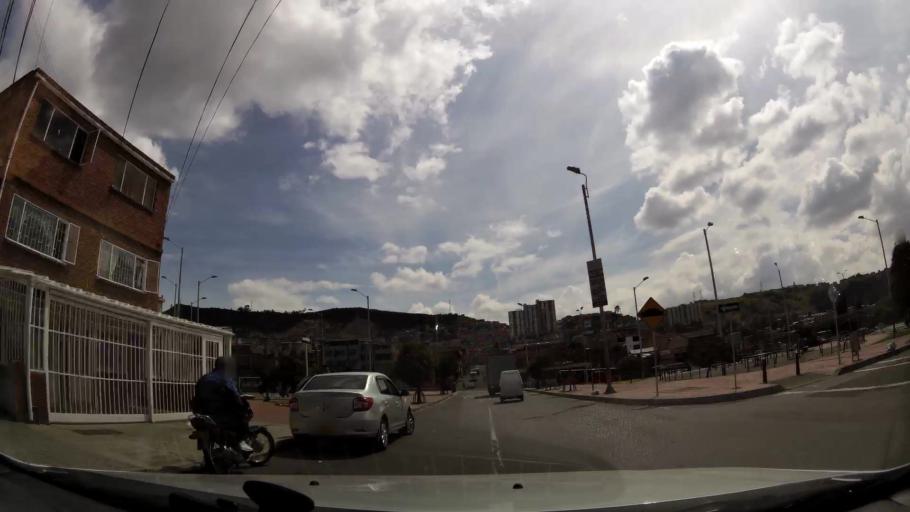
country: CO
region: Bogota D.C.
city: Bogota
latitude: 4.5685
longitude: -74.0996
